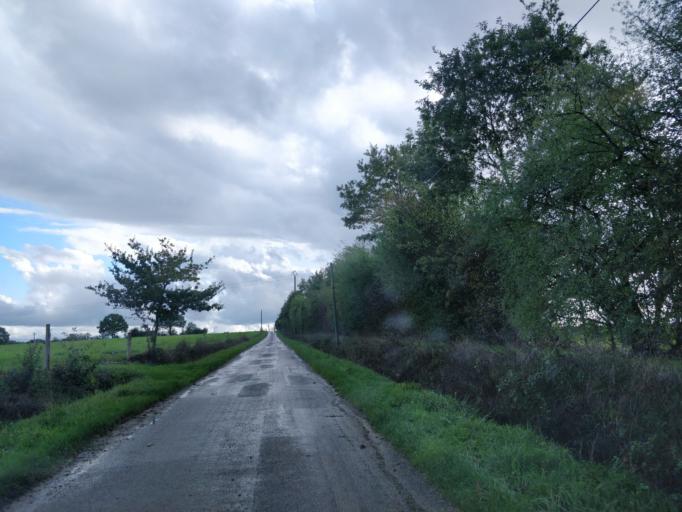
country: FR
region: Brittany
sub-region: Departement d'Ille-et-Vilaine
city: Chateaubourg
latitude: 48.1284
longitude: -1.4257
